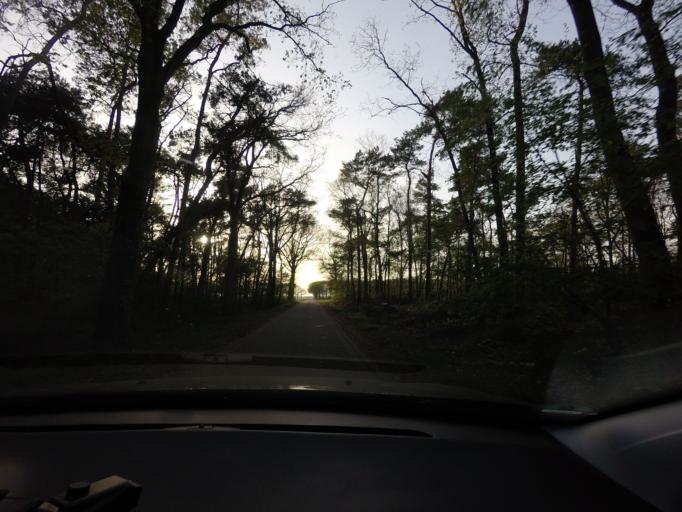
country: NL
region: North Brabant
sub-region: Gemeente Baarle-Nassau
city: Baarle-Nassau
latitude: 51.5081
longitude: 4.9674
